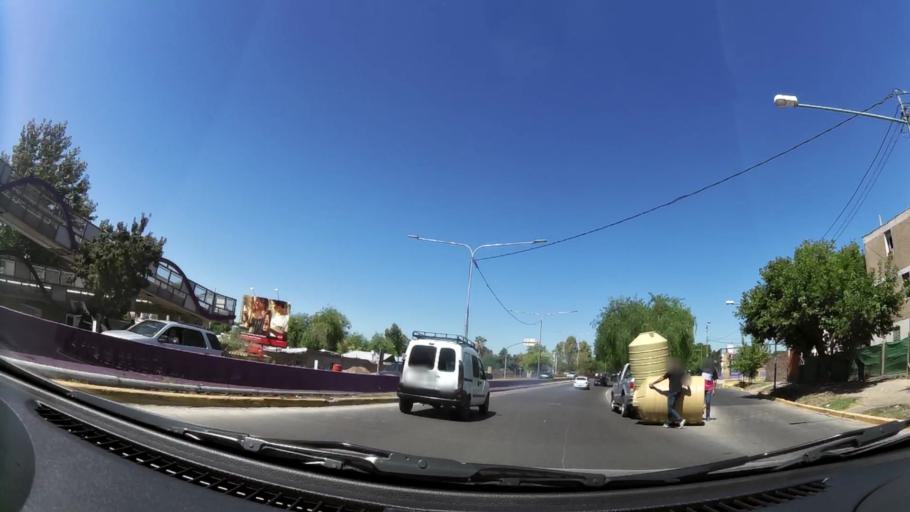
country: AR
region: Mendoza
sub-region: Departamento de Godoy Cruz
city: Godoy Cruz
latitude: -32.9248
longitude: -68.8638
